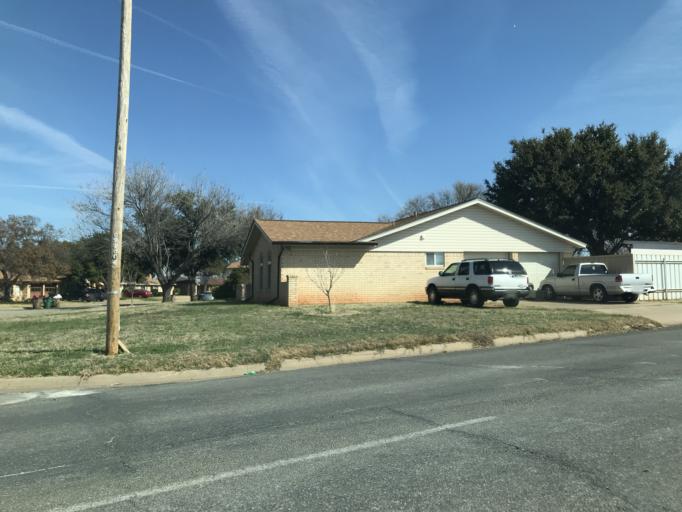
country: US
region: Texas
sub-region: Tom Green County
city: San Angelo
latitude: 31.4358
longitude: -100.4925
